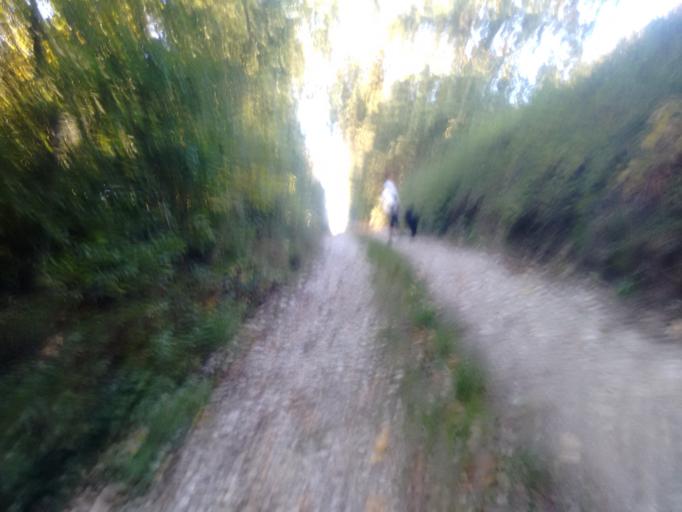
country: AT
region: Upper Austria
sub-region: Wels Stadt
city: Wels
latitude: 48.1852
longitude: 13.9918
